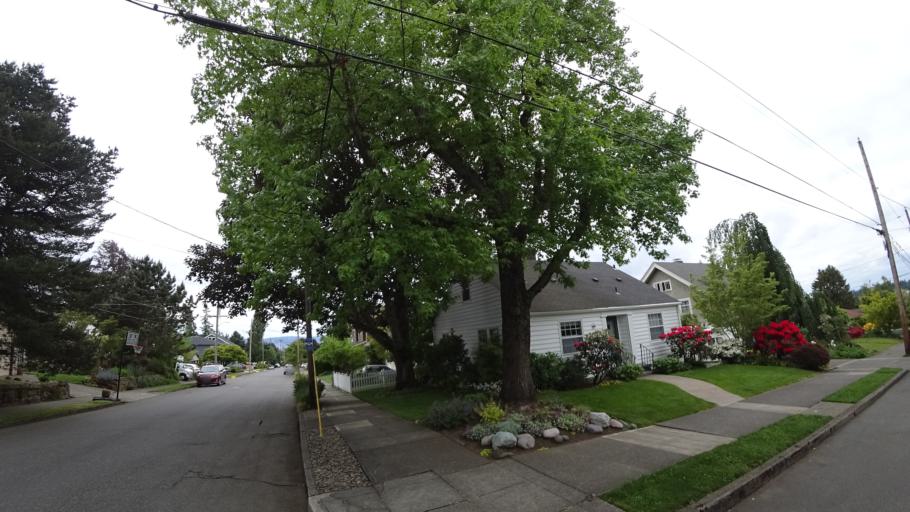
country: US
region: Oregon
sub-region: Multnomah County
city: Lents
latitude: 45.5175
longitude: -122.6042
